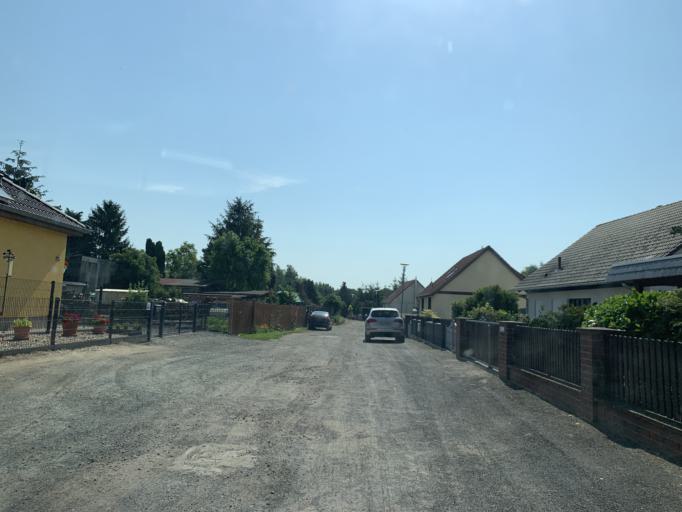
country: DE
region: Saxony-Anhalt
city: Erxleben
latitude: 52.2183
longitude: 11.2334
